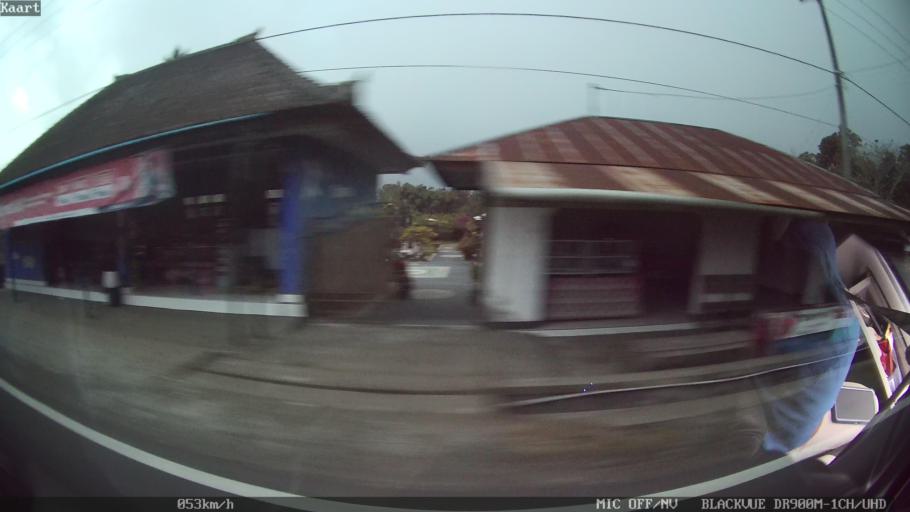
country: ID
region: Bali
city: Banjar Kedisan
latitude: -8.2865
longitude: 115.3197
